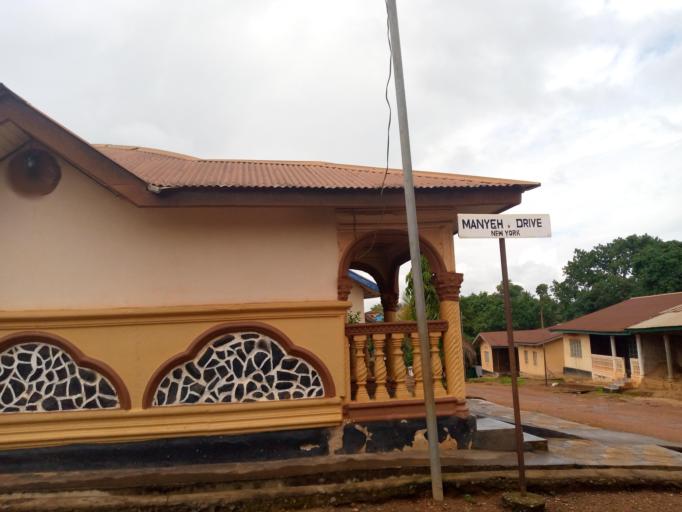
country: SL
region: Eastern Province
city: Kenema
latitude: 7.8741
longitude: -11.1792
